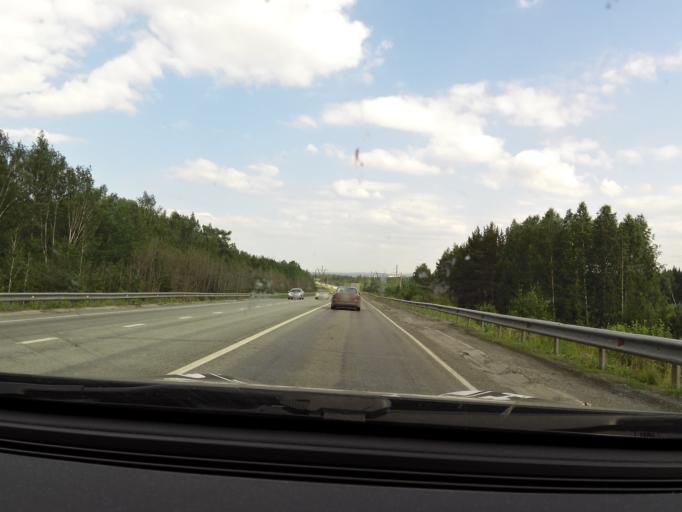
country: RU
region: Sverdlovsk
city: Revda
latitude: 56.8297
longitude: 59.8535
